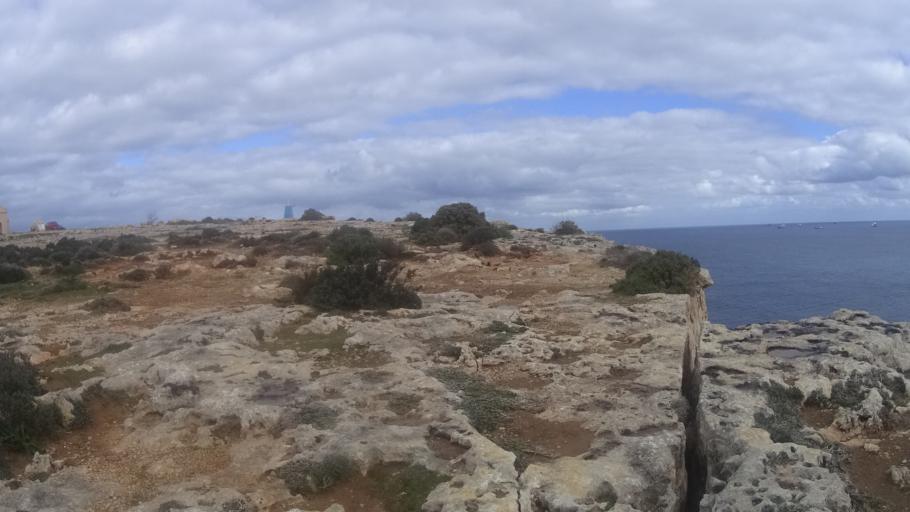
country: MT
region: Il-Mellieha
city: Mellieha
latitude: 35.9876
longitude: 14.3753
